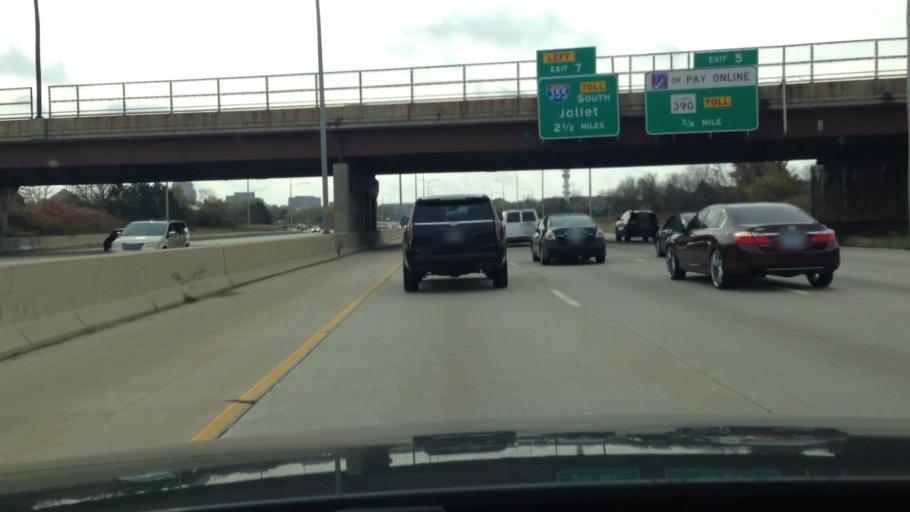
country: US
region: Illinois
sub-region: DuPage County
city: Itasca
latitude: 42.0039
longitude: -88.0270
